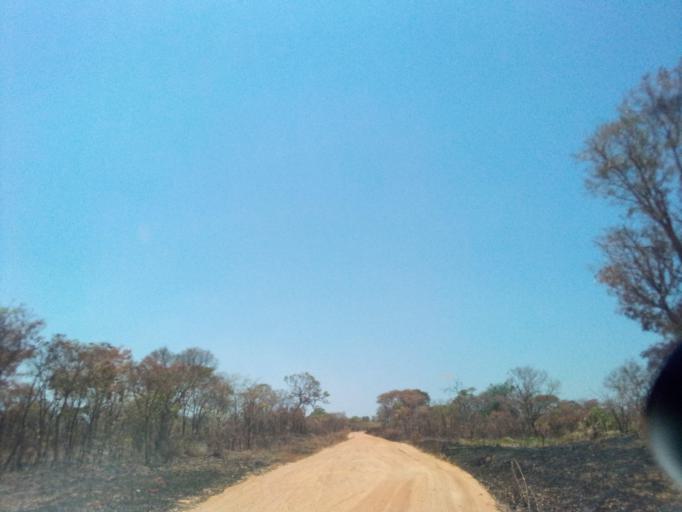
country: ZM
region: Northern
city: Mpika
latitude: -12.2540
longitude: 30.6810
